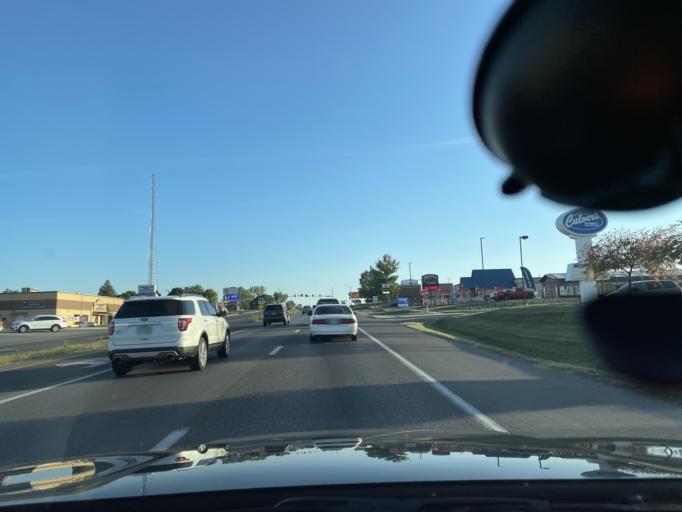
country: US
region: Missouri
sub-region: Andrew County
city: Country Club Village
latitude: 39.8053
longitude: -94.8153
